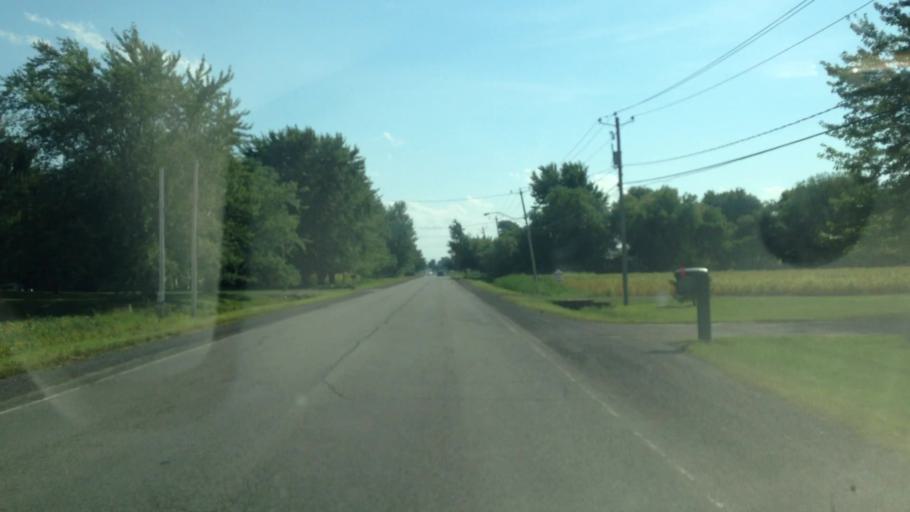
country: CA
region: Quebec
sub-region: Monteregie
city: Mercier
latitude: 45.2825
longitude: -73.6892
